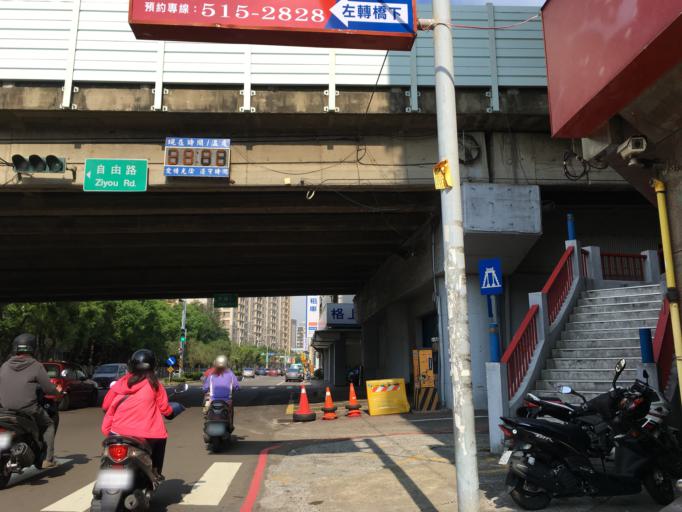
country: TW
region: Taiwan
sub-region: Hsinchu
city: Hsinchu
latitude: 24.8094
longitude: 120.9834
